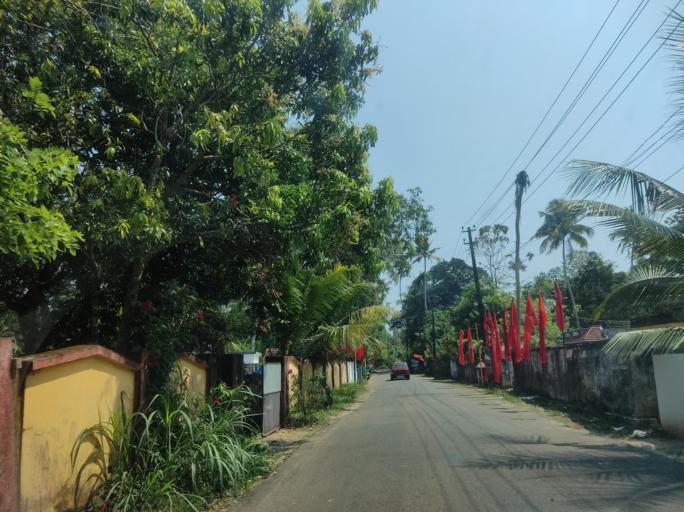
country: IN
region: Kerala
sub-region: Alappuzha
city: Vayalar
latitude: 9.6920
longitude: 76.3030
